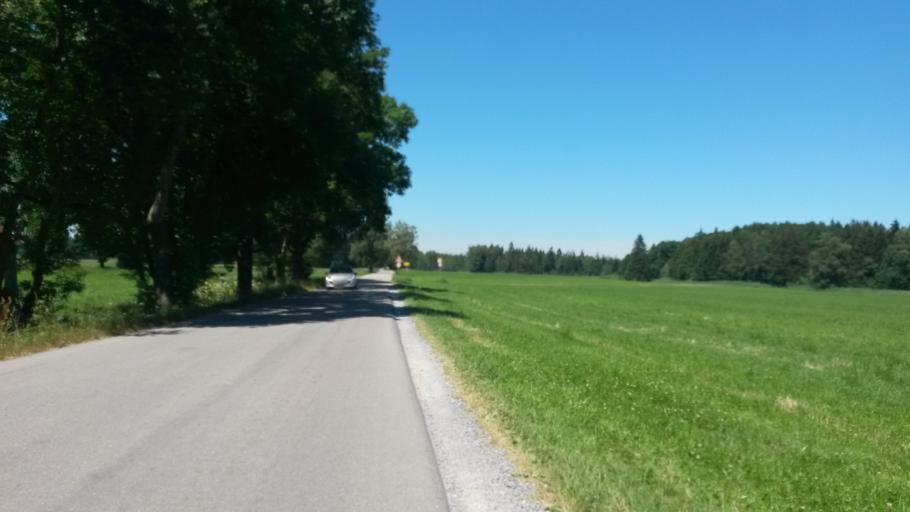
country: DE
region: Bavaria
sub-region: Upper Bavaria
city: Bernau am Chiemsee
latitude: 47.8017
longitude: 12.4058
